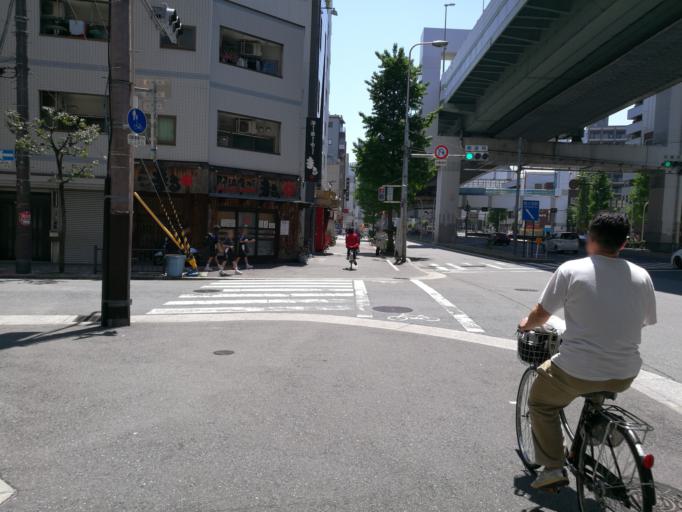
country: JP
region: Osaka
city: Osaka-shi
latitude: 34.6833
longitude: 135.4858
